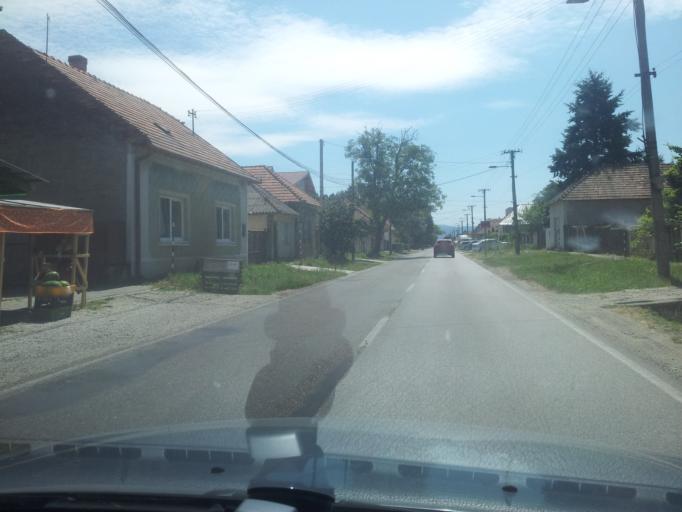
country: SK
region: Nitriansky
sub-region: Okres Nove Zamky
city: Sturovo
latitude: 47.8181
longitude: 18.6931
